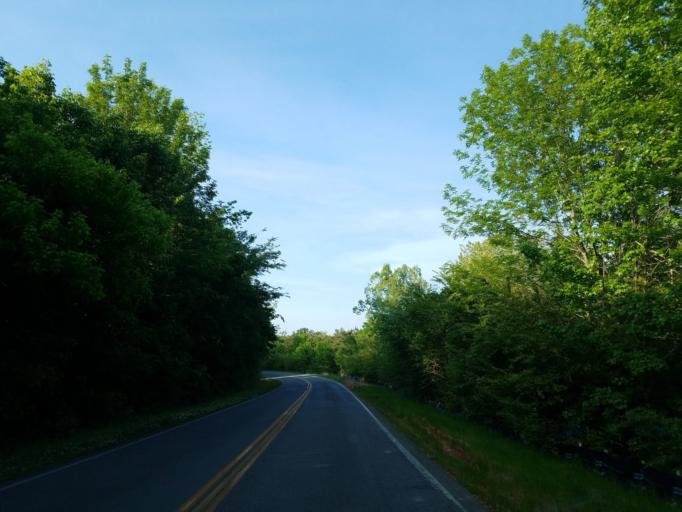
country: US
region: Georgia
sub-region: Floyd County
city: Shannon
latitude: 34.4747
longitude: -85.1380
